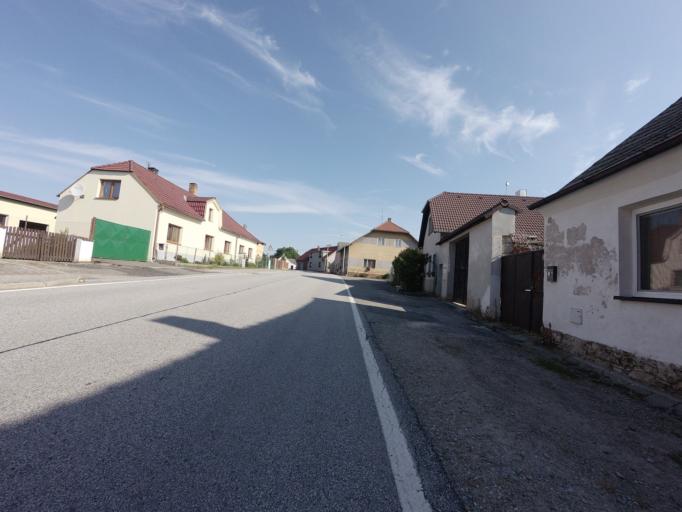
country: CZ
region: Jihocesky
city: Bernartice
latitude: 49.2971
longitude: 14.3876
